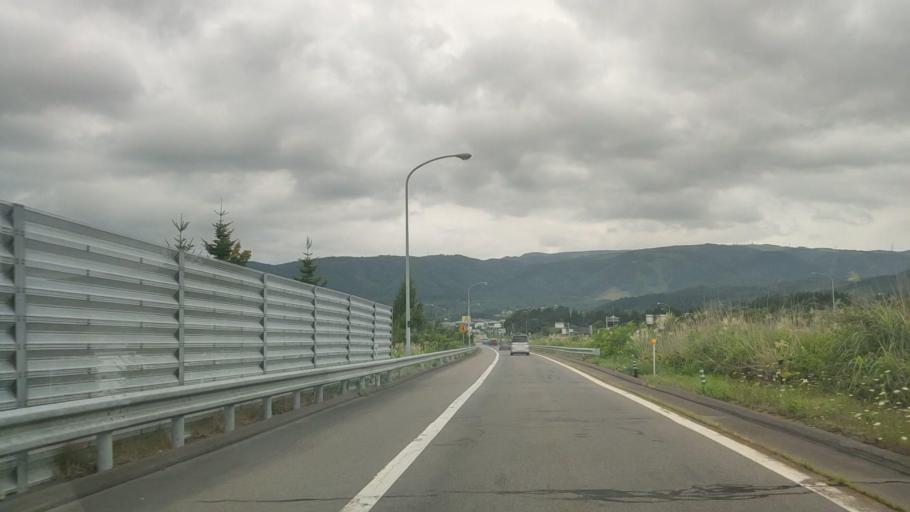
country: JP
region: Hokkaido
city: Nanae
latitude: 41.9224
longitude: 140.6707
